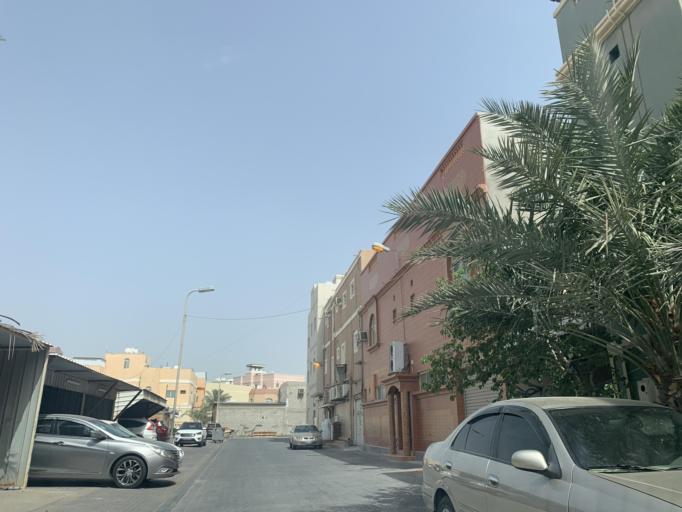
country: BH
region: Northern
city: Madinat `Isa
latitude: 26.1827
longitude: 50.5252
